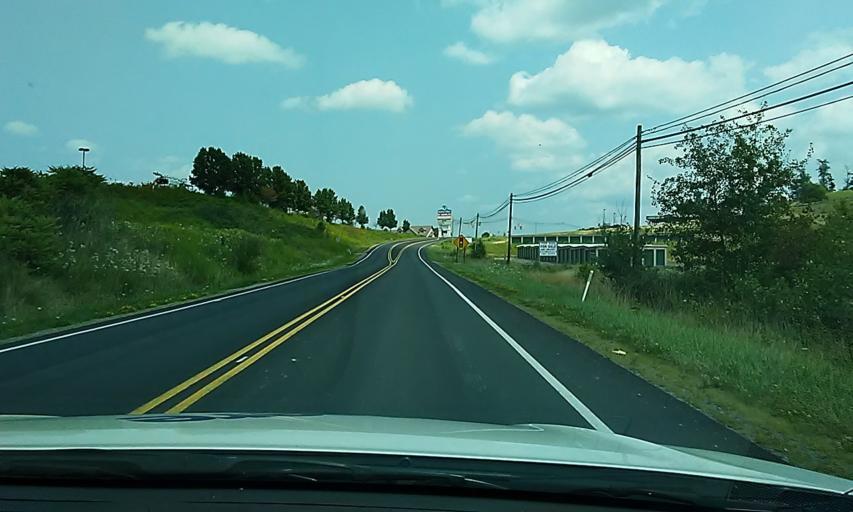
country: US
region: Pennsylvania
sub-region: Elk County
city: Saint Marys
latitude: 41.4306
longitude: -78.5217
